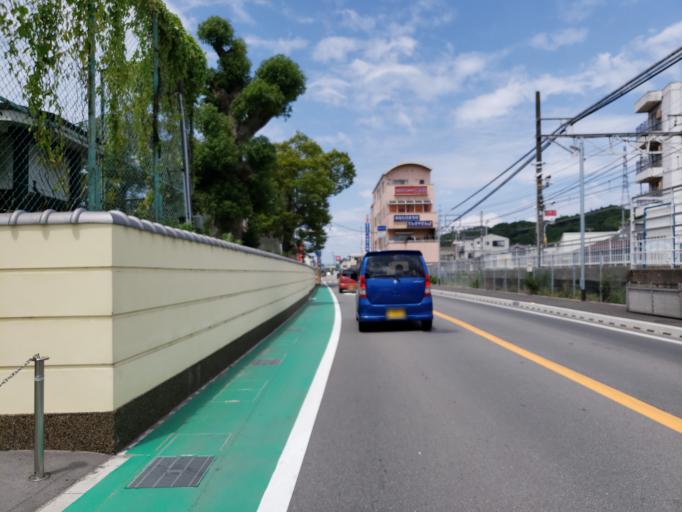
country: JP
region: Hyogo
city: Shirahamacho-usazakiminami
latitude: 34.7868
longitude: 134.7069
